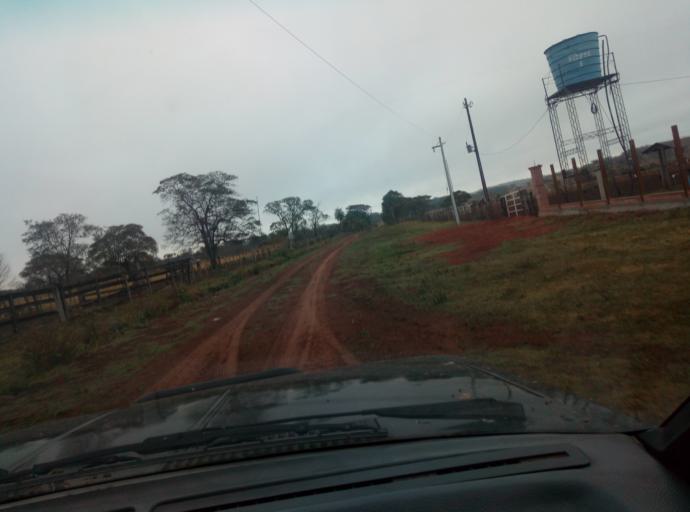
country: PY
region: Caaguazu
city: Carayao
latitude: -25.1938
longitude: -56.3264
